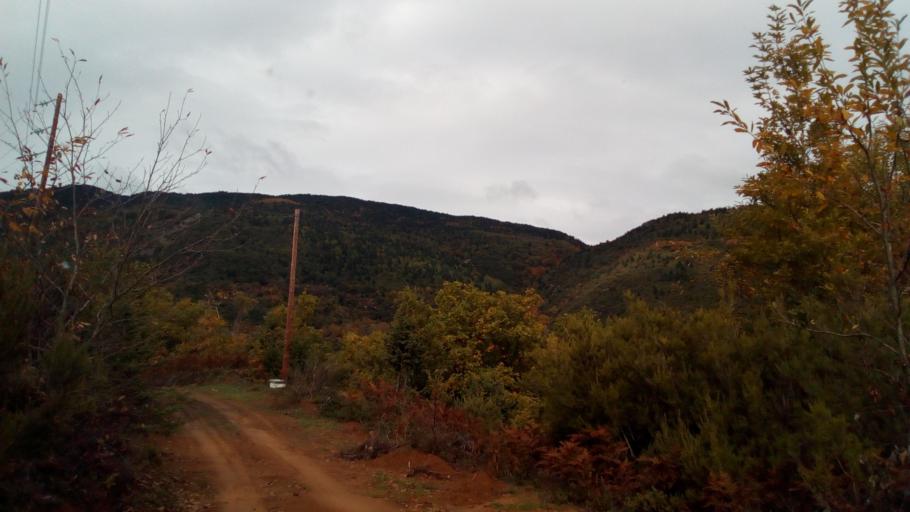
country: GR
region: West Greece
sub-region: Nomos Aitolias kai Akarnanias
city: Nafpaktos
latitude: 38.5582
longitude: 21.9648
